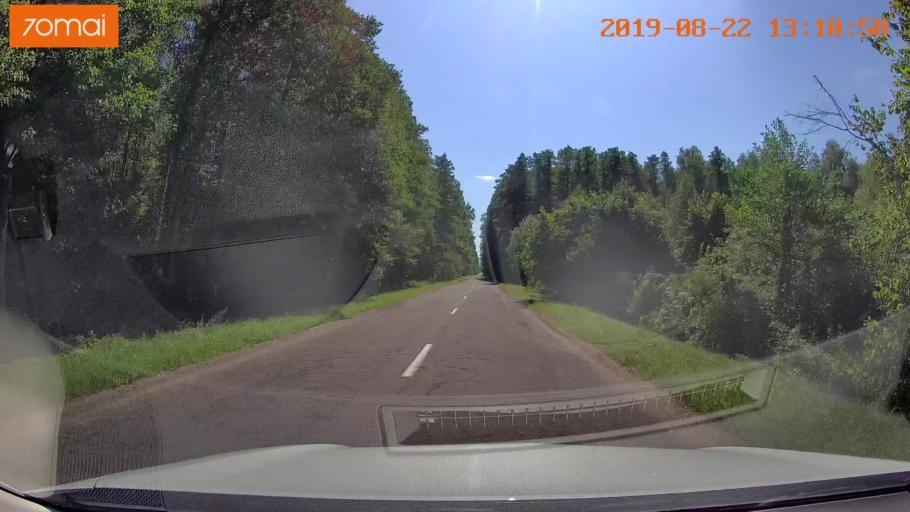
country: BY
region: Minsk
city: Prawdzinski
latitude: 53.2895
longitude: 27.8503
